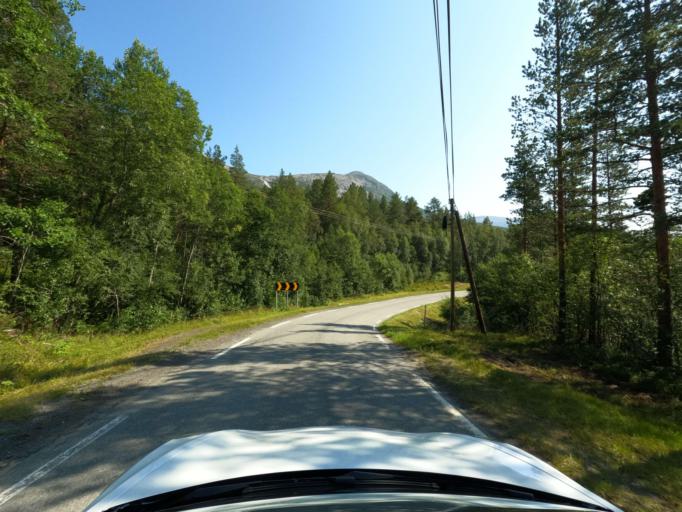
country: NO
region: Nordland
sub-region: Narvik
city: Narvik
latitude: 68.1952
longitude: 17.5560
